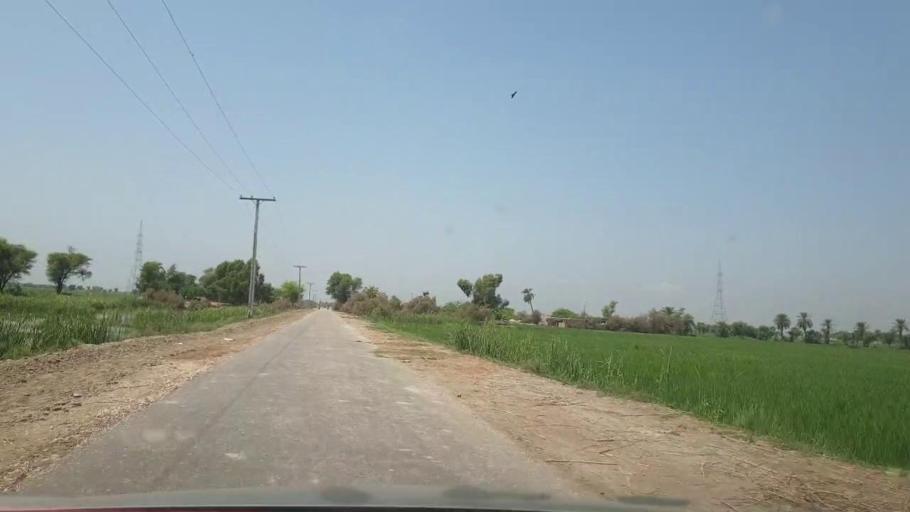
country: PK
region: Sindh
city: Warah
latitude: 27.4833
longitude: 67.7472
